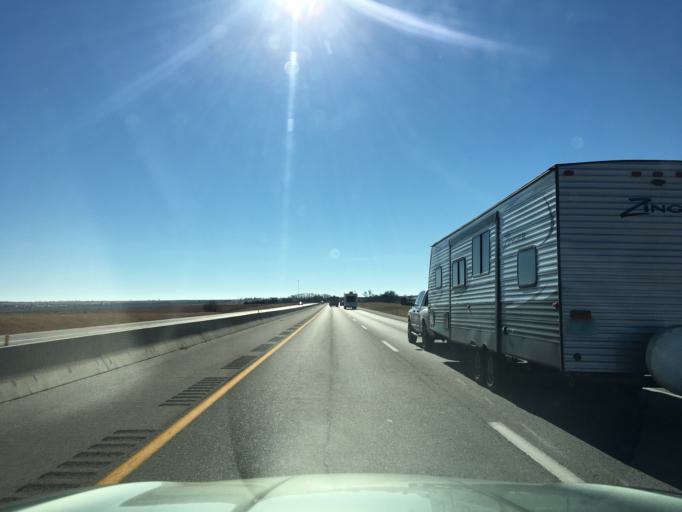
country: US
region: Oklahoma
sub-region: Kay County
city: Blackwell
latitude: 37.0210
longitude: -97.3382
